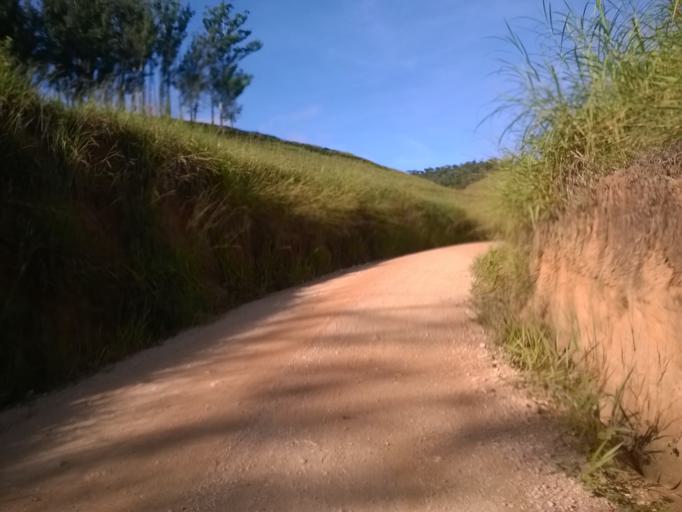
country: BR
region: Minas Gerais
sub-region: Uba
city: Uba
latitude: -21.0874
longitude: -43.0061
